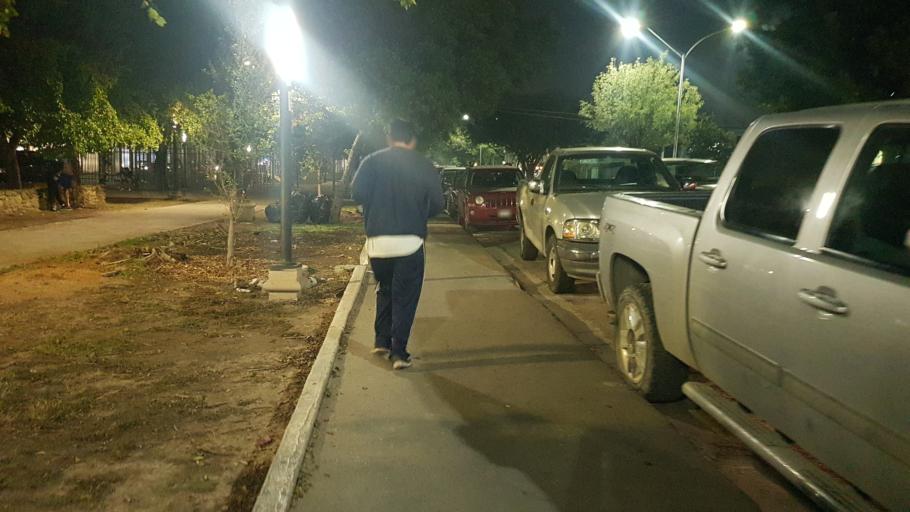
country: MX
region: Nuevo Leon
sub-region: San Nicolas de los Garza
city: San Nicolas de los Garza
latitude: 25.7421
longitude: -100.2757
